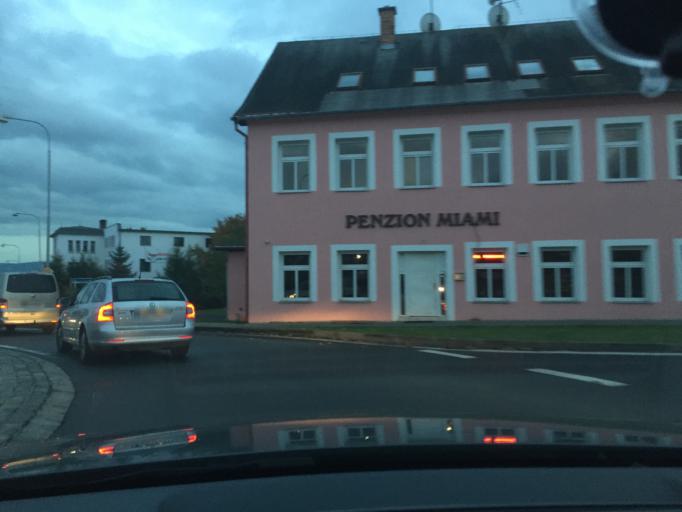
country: CZ
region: Ustecky
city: Novosedlice
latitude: 50.6586
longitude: 13.8040
